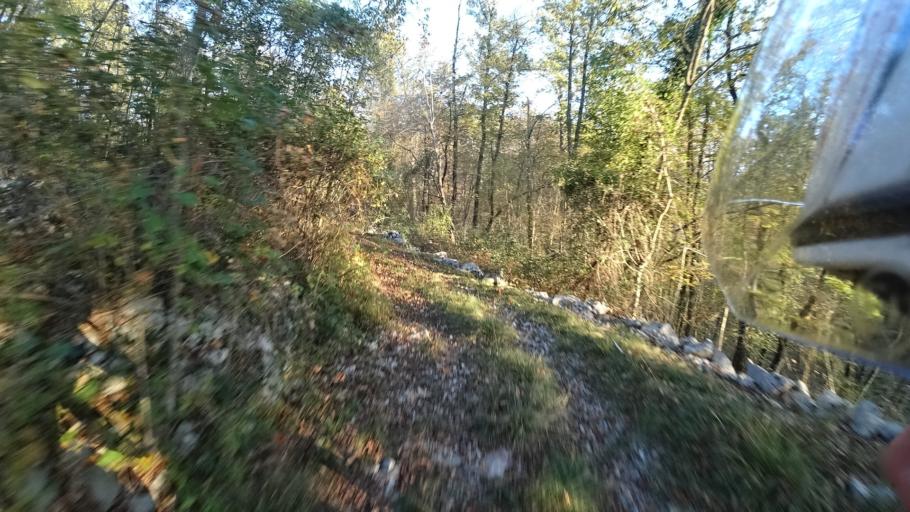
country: HR
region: Primorsko-Goranska
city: Kastav
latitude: 45.4066
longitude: 14.3158
